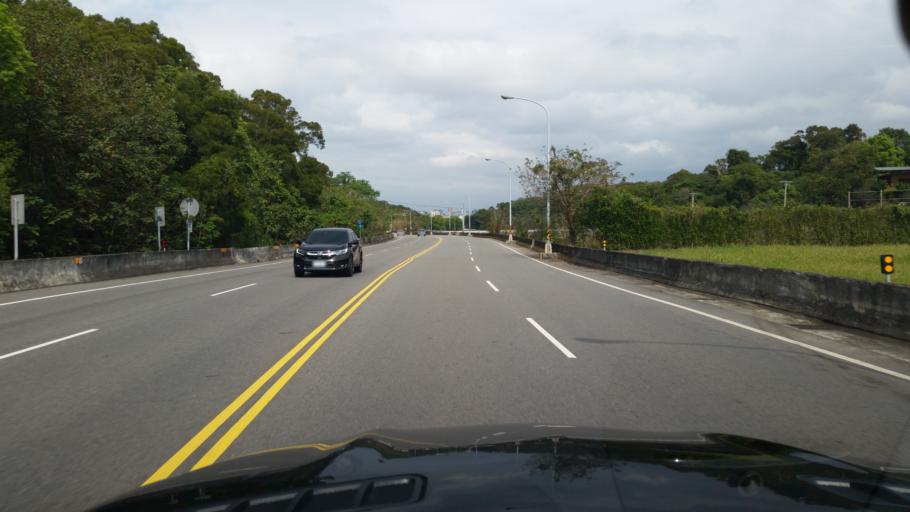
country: TW
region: Taiwan
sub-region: Miaoli
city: Miaoli
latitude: 24.6438
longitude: 120.8600
